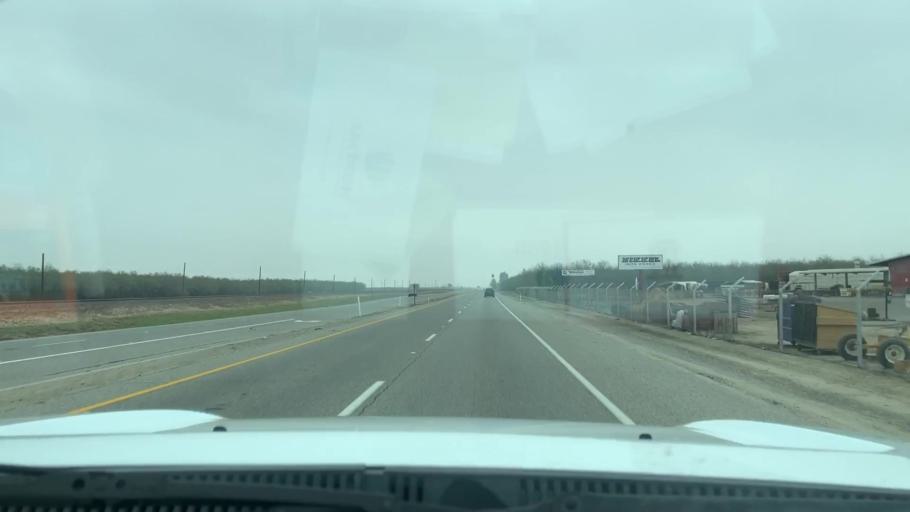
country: US
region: California
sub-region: Kern County
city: Shafter
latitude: 35.5343
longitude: -119.3127
